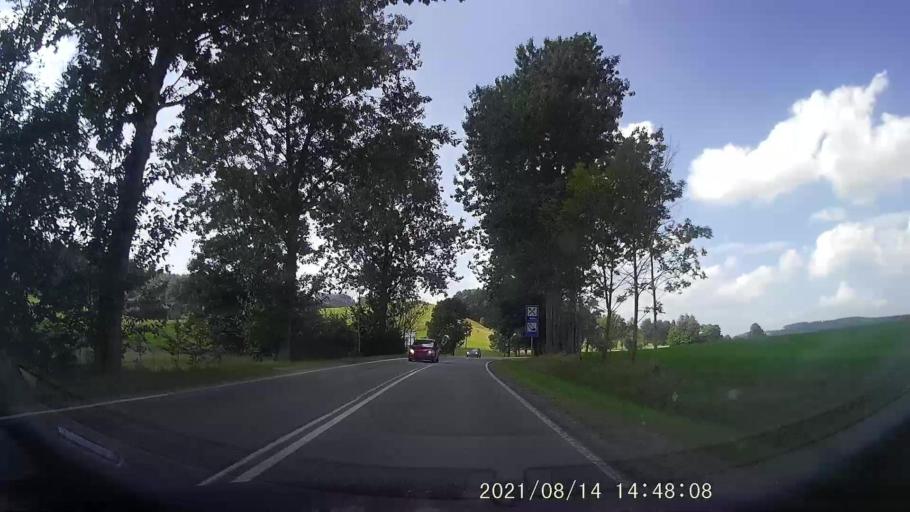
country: PL
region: Lower Silesian Voivodeship
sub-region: Powiat walbrzyski
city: Gluszyca Gorna
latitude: 50.6293
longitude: 16.4001
